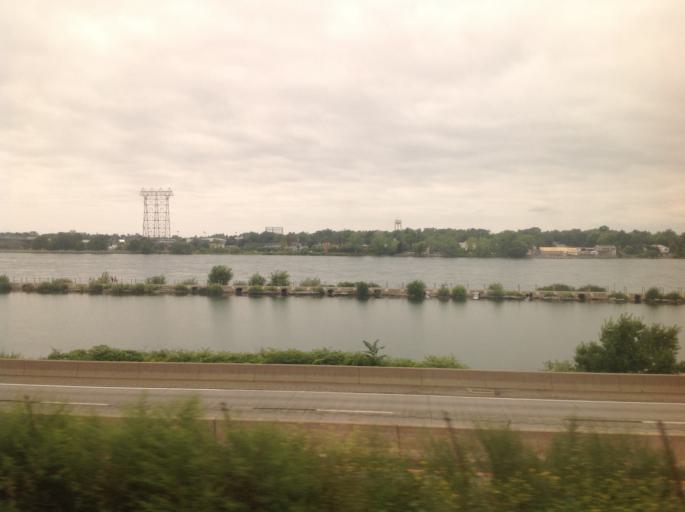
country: CA
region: Ontario
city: Fort Erie
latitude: 42.9123
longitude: -78.9013
